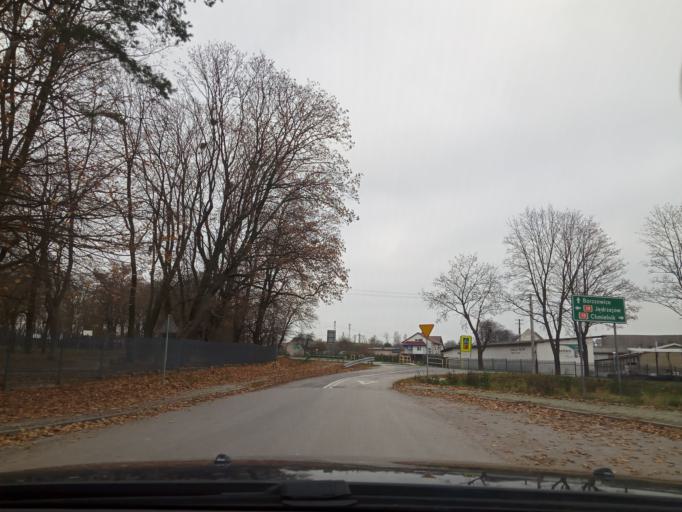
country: PL
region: Swietokrzyskie
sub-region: Powiat jedrzejowski
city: Imielno
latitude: 50.6047
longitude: 20.4907
